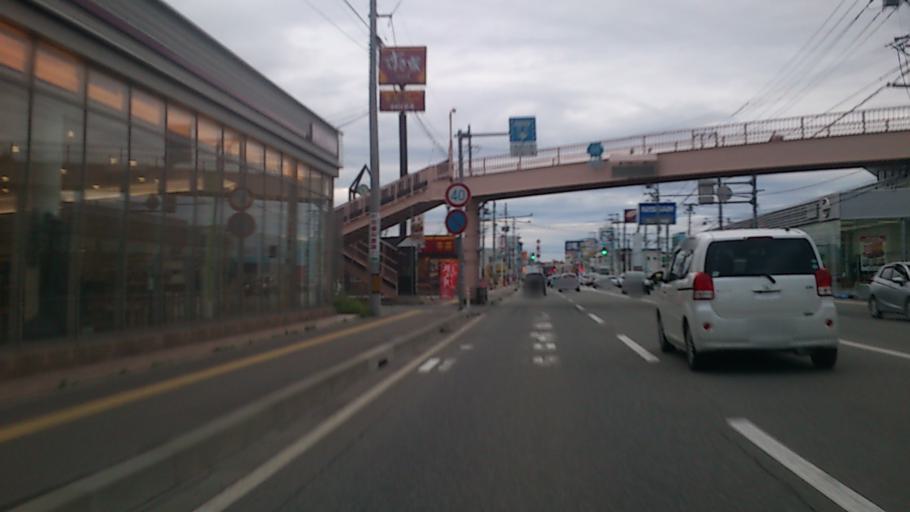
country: JP
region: Akita
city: Akita Shi
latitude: 39.7322
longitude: 140.1019
